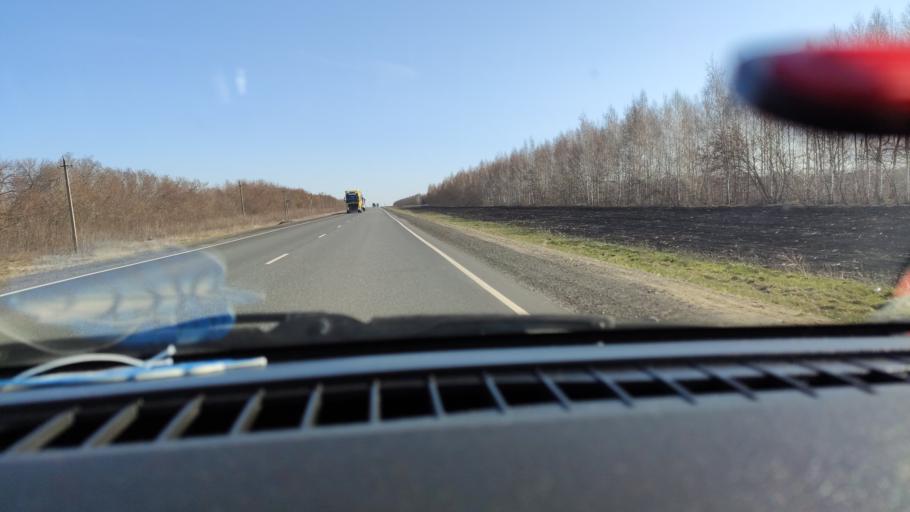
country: RU
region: Samara
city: Syzran'
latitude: 52.9818
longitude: 48.3140
